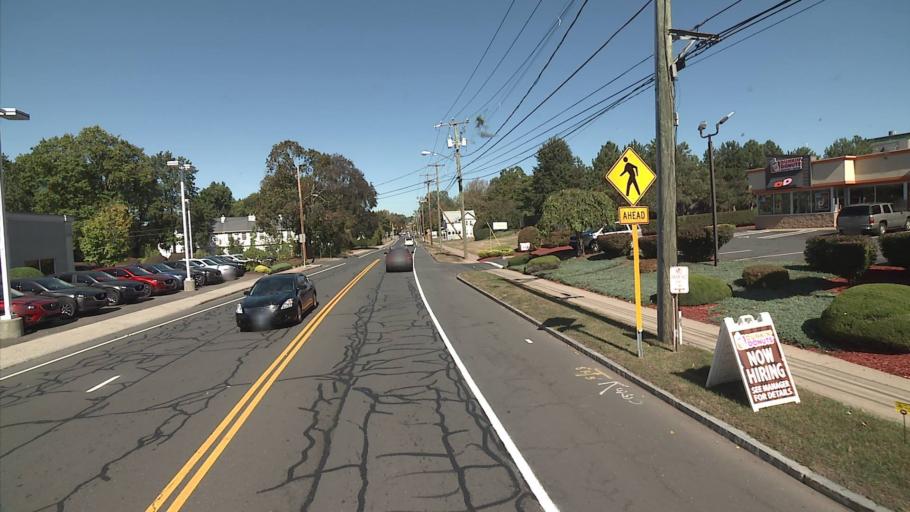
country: US
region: Connecticut
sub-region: Hartford County
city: Manchester
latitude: 41.7962
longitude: -72.5212
